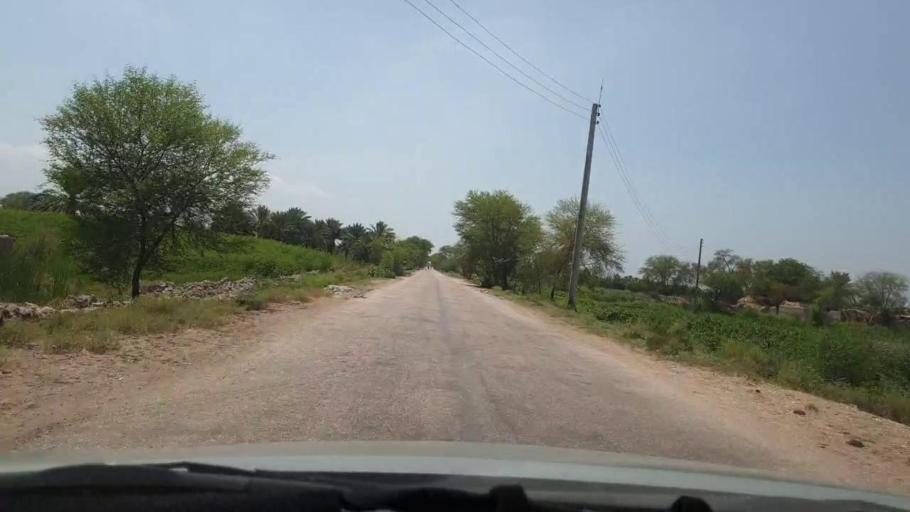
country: PK
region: Sindh
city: Pano Aqil
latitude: 27.6635
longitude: 69.1409
